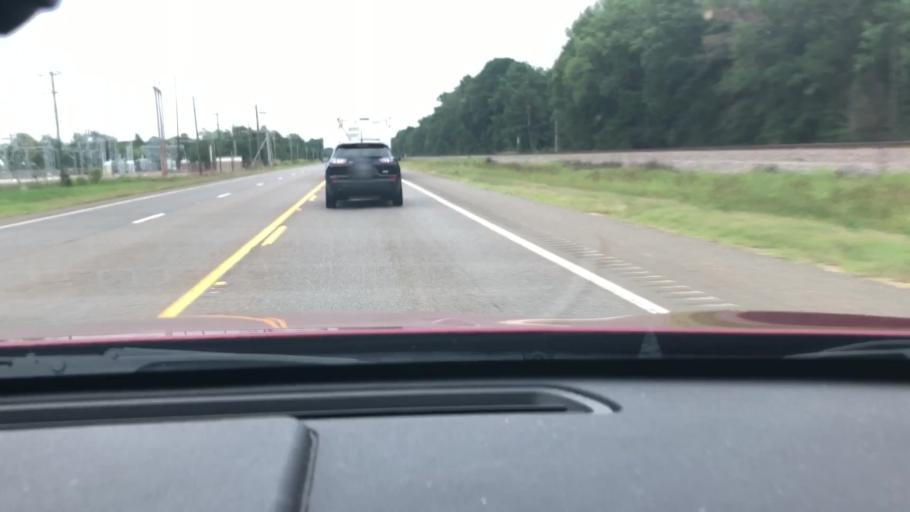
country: US
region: Arkansas
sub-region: Lafayette County
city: Lewisville
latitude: 33.3577
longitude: -93.6016
